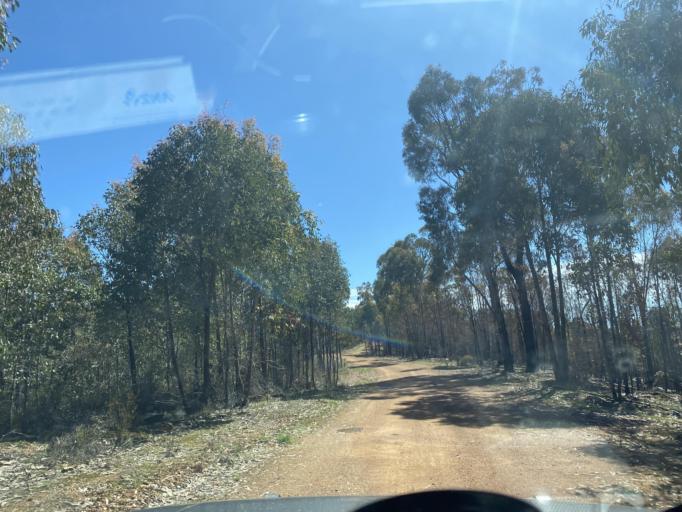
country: AU
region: Victoria
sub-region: Benalla
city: Benalla
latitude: -36.7353
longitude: 146.1822
